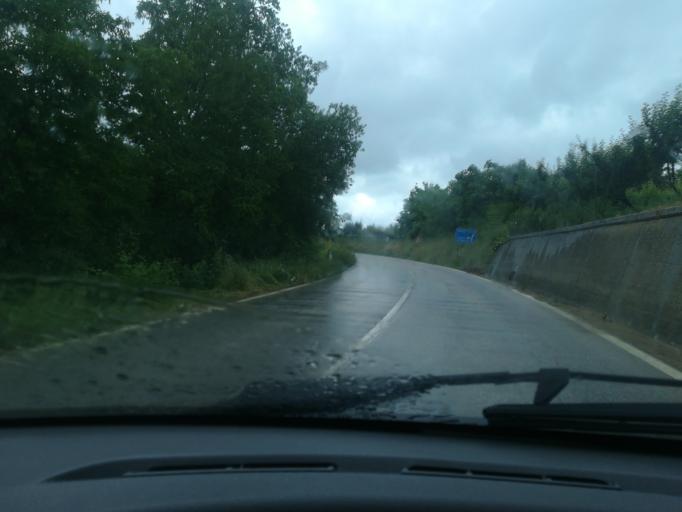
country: IT
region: The Marches
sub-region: Province of Fermo
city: Amandola
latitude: 42.9977
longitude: 13.3383
